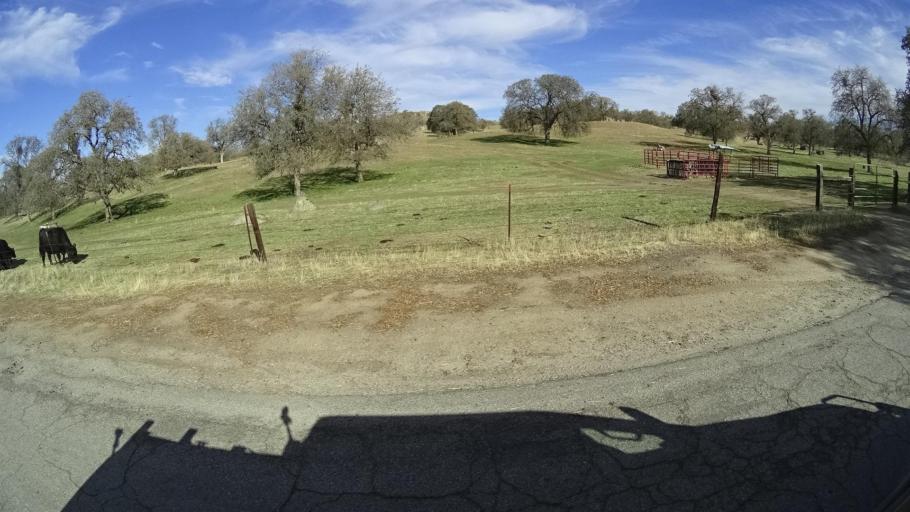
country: US
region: California
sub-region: Kern County
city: Oildale
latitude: 35.5823
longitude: -118.8210
